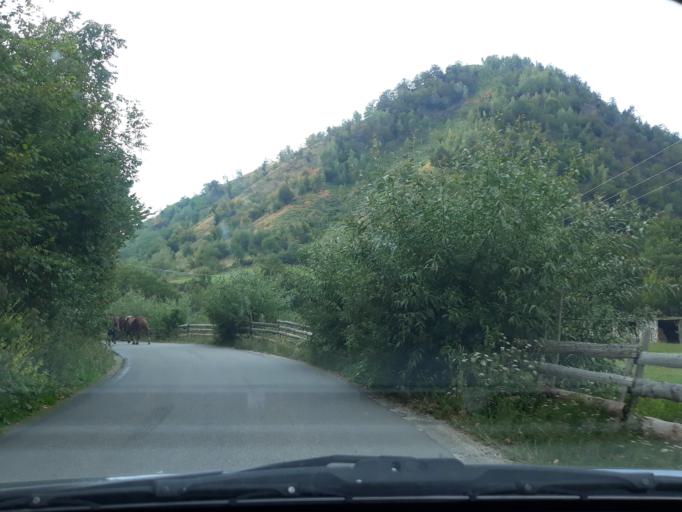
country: RO
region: Bihor
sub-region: Comuna Pietroasa
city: Pietroasa
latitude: 46.5898
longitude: 22.5831
